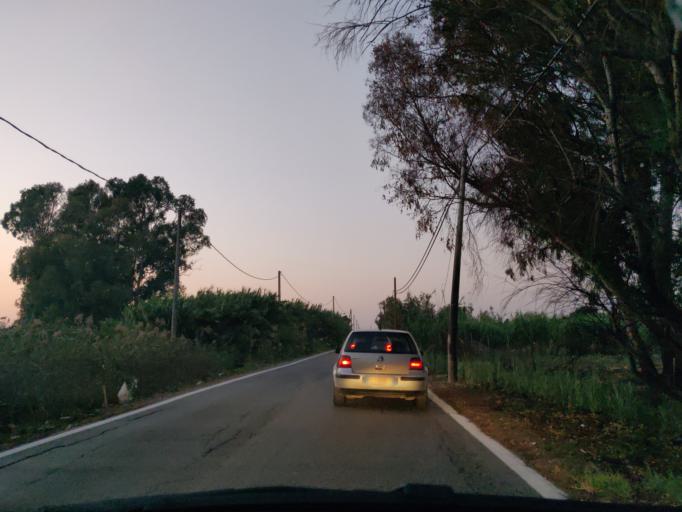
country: IT
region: Latium
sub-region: Citta metropolitana di Roma Capitale
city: Npp 23 (Parco Leonardo)
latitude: 41.8264
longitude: 12.2888
